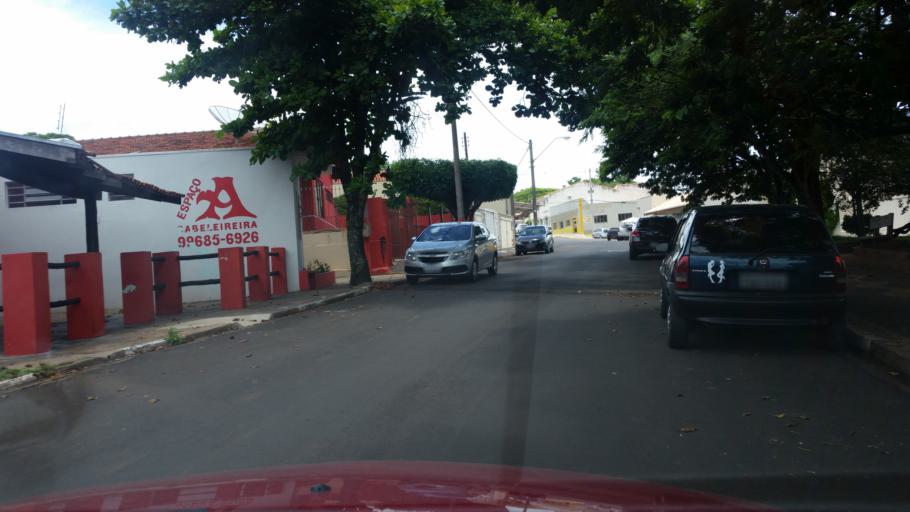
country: BR
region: Sao Paulo
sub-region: Itai
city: Itai
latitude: -23.4222
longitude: -49.0911
